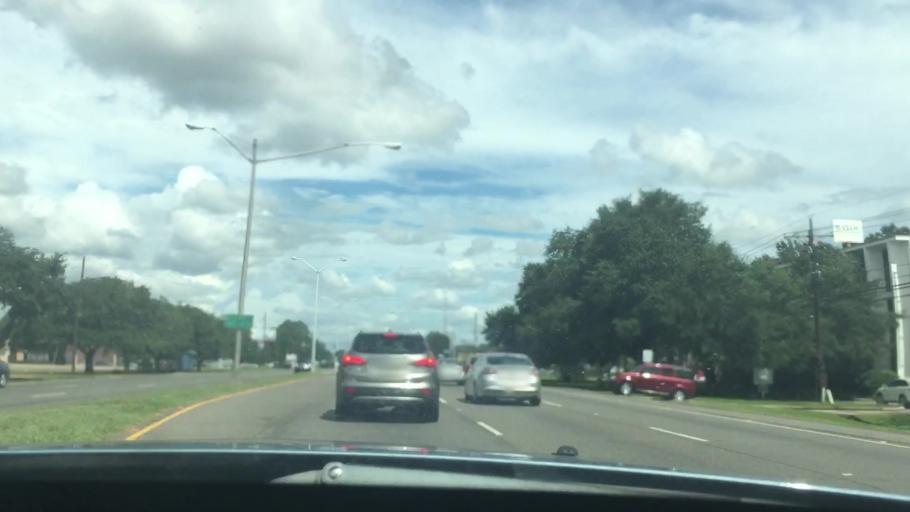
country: US
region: Louisiana
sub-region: East Baton Rouge Parish
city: Baton Rouge
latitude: 30.4510
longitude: -91.1331
